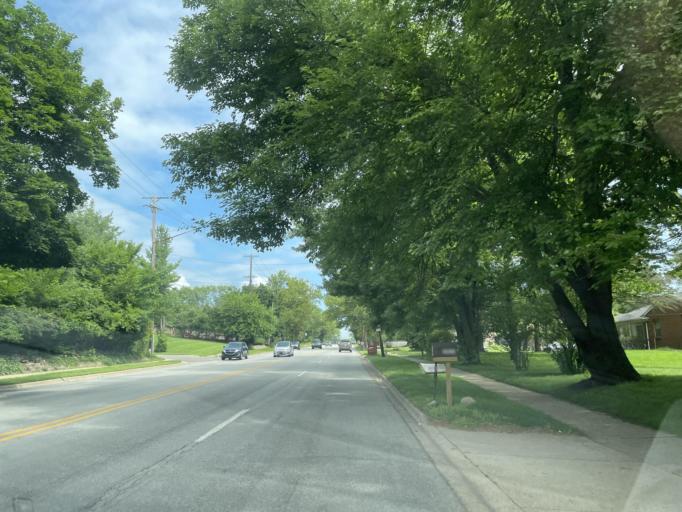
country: US
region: Michigan
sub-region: Kent County
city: East Grand Rapids
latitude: 42.9071
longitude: -85.6273
